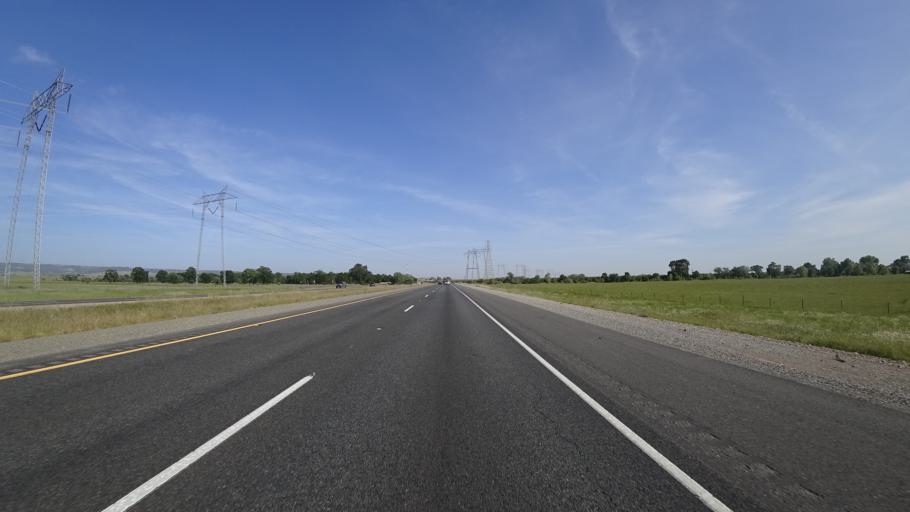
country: US
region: California
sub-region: Butte County
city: Durham
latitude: 39.6105
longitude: -121.6758
